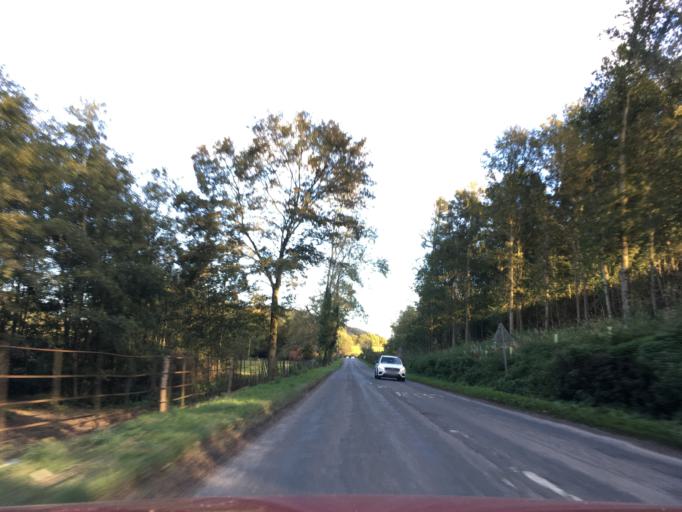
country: GB
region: England
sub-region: Herefordshire
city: Donnington
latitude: 52.0280
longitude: -2.3733
